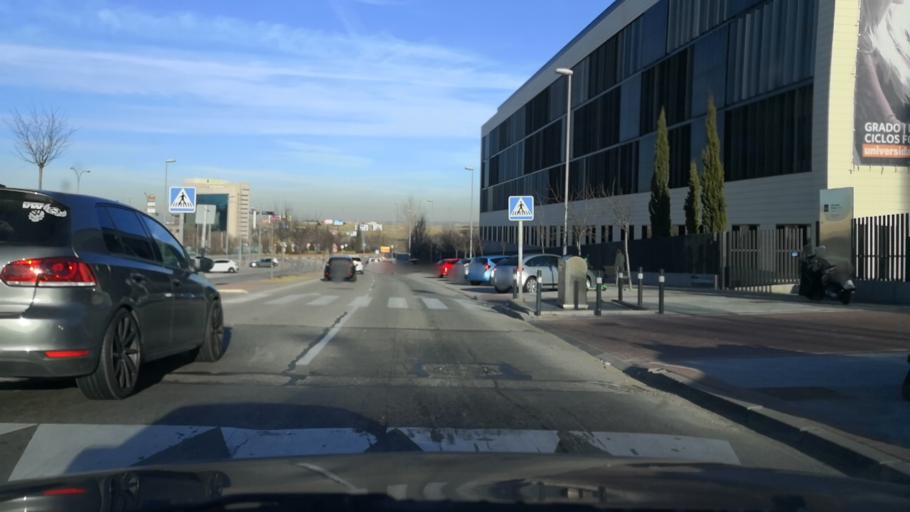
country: ES
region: Madrid
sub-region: Provincia de Madrid
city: San Sebastian de los Reyes
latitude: 40.5350
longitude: -3.6175
